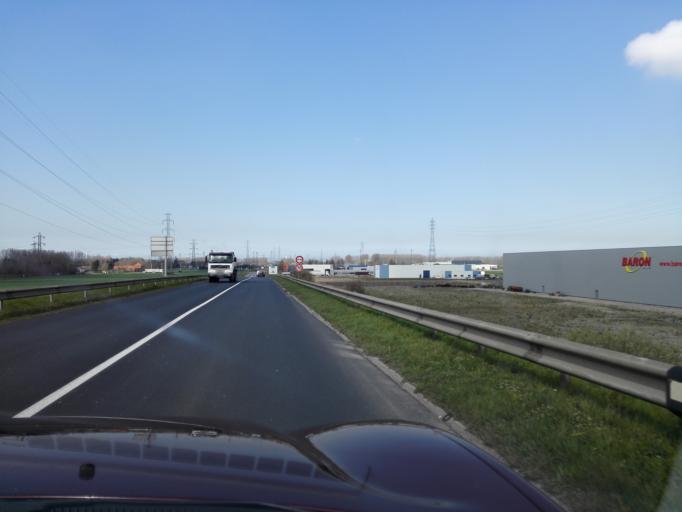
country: FR
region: Nord-Pas-de-Calais
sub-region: Departement du Nord
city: Grande-Synthe
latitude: 50.9883
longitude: 2.3007
